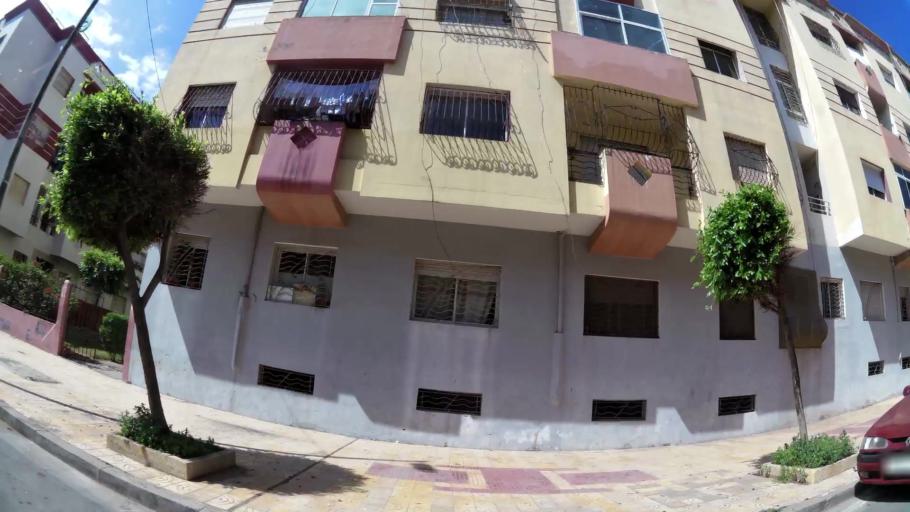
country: MA
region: Rabat-Sale-Zemmour-Zaer
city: Sale
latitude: 34.0780
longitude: -6.7914
